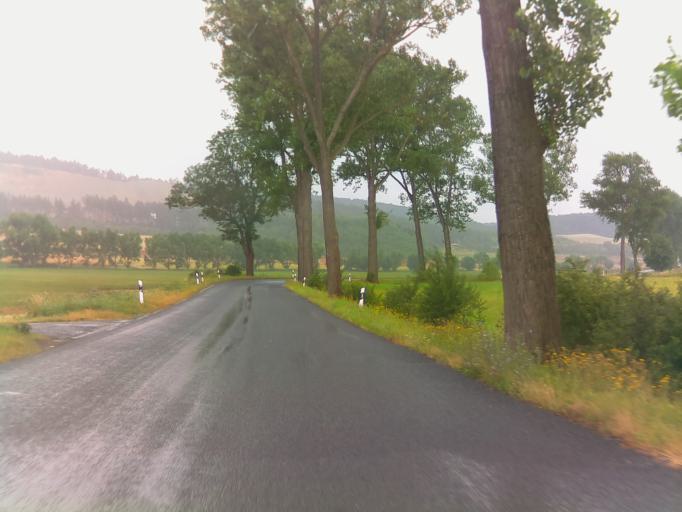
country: DE
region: Thuringia
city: Stadtilm
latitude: 50.7500
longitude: 11.1091
